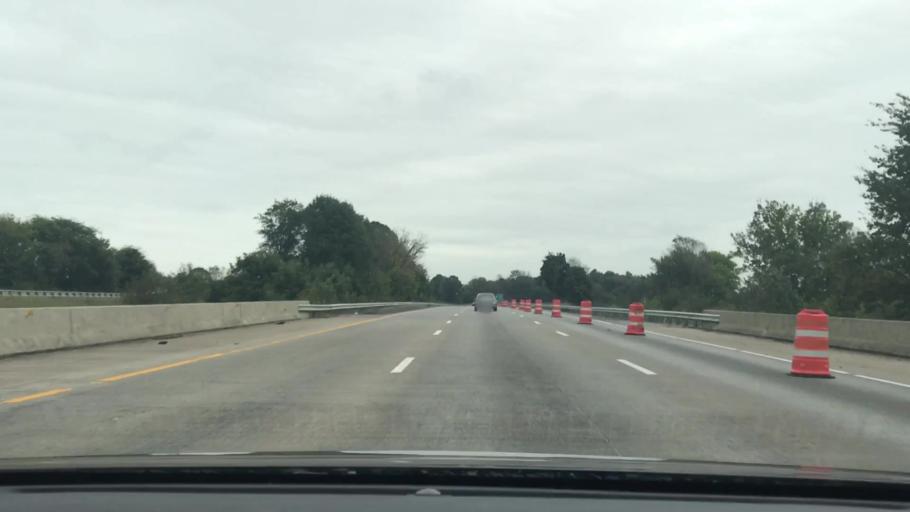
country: US
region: Kentucky
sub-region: Edmonson County
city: Brownsville
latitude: 37.0188
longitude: -86.2608
